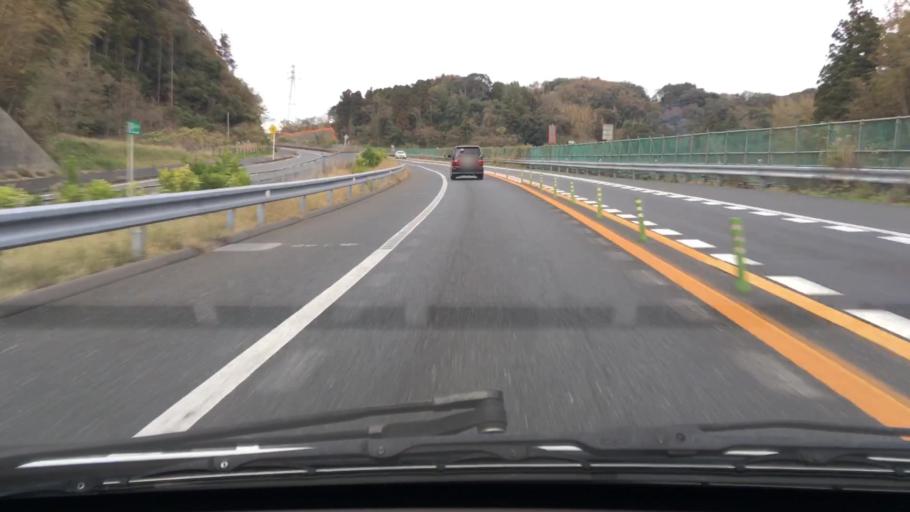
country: JP
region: Chiba
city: Kimitsu
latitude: 35.2268
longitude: 139.8858
